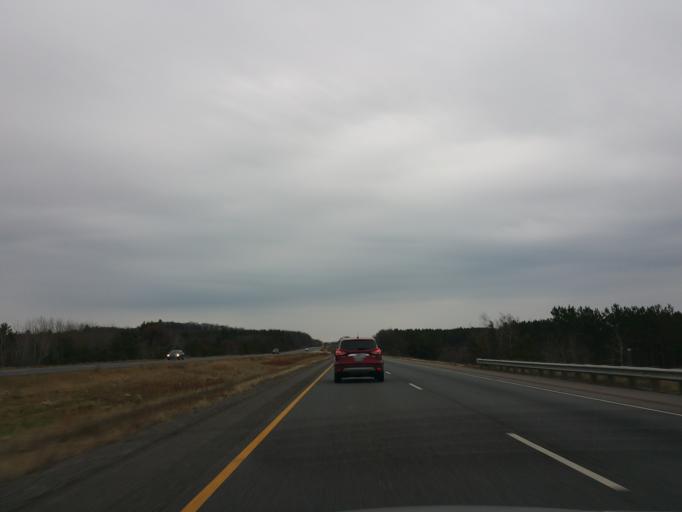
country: US
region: Wisconsin
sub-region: Jackson County
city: Black River Falls
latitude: 44.2748
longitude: -90.7970
